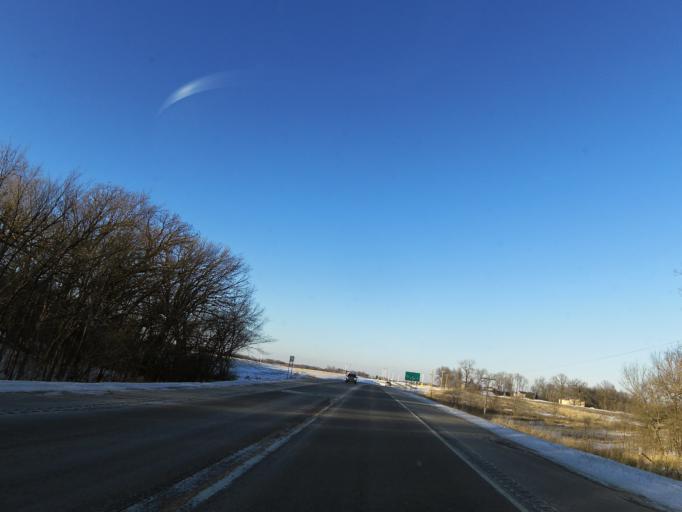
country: US
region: Minnesota
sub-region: Rice County
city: Lonsdale
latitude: 44.5398
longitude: -93.4428
